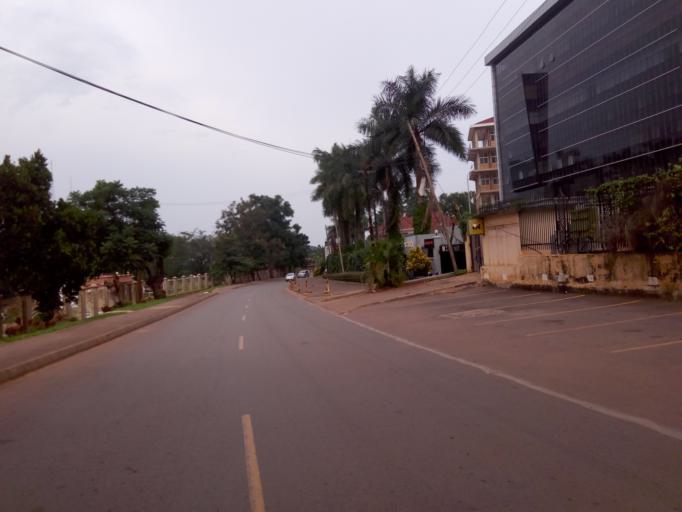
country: UG
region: Central Region
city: Kampala Central Division
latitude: 0.3318
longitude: 32.5780
